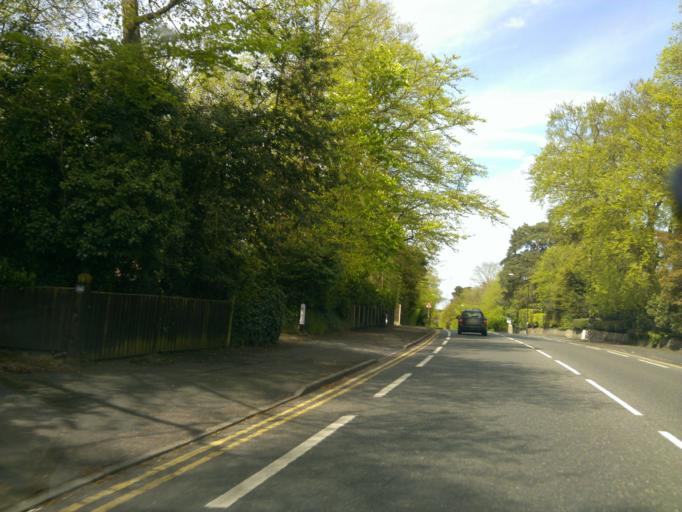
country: GB
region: England
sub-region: Essex
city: West Bergholt
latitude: 51.8895
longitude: 0.8721
